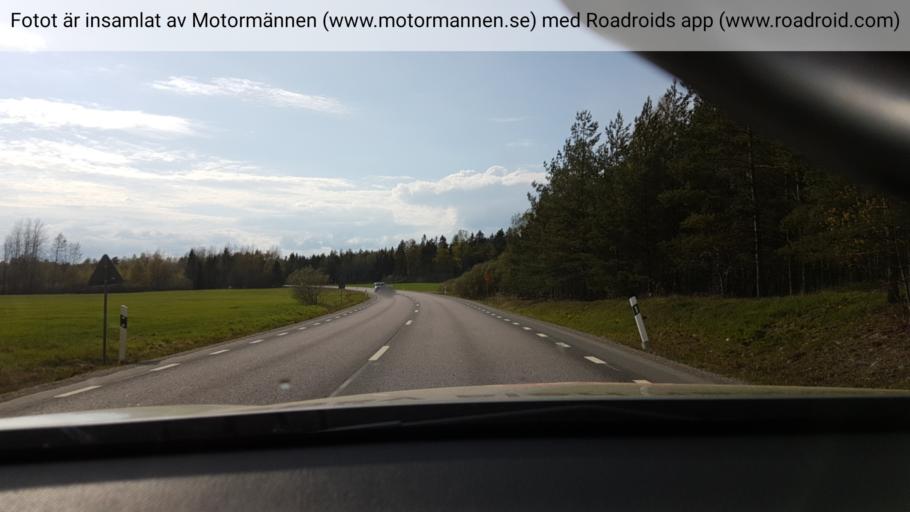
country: SE
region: Stockholm
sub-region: Nynashamns Kommun
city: Osmo
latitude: 58.9829
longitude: 17.8742
